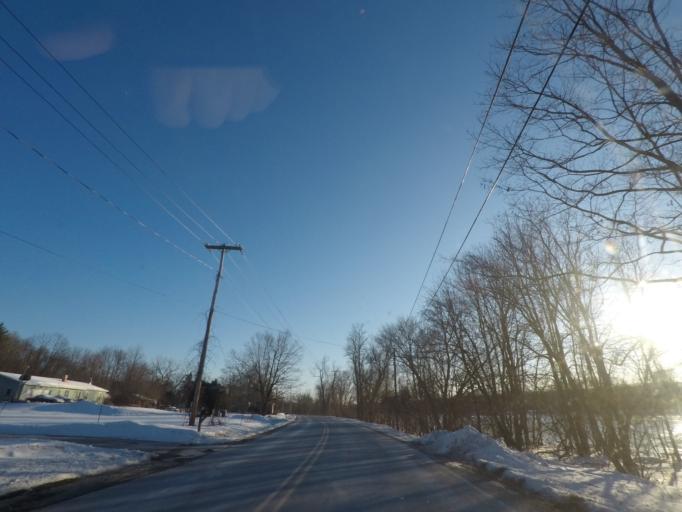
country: US
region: New York
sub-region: Saratoga County
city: Mechanicville
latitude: 42.8723
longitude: -73.6716
